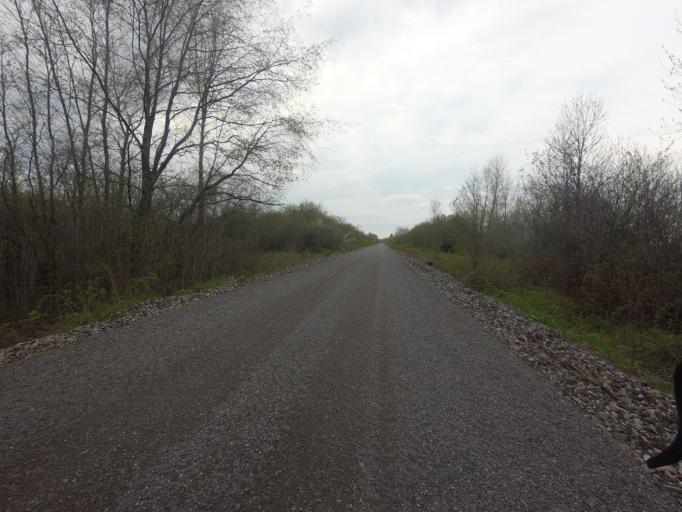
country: CA
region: Ontario
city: Carleton Place
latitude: 45.2134
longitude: -76.1796
